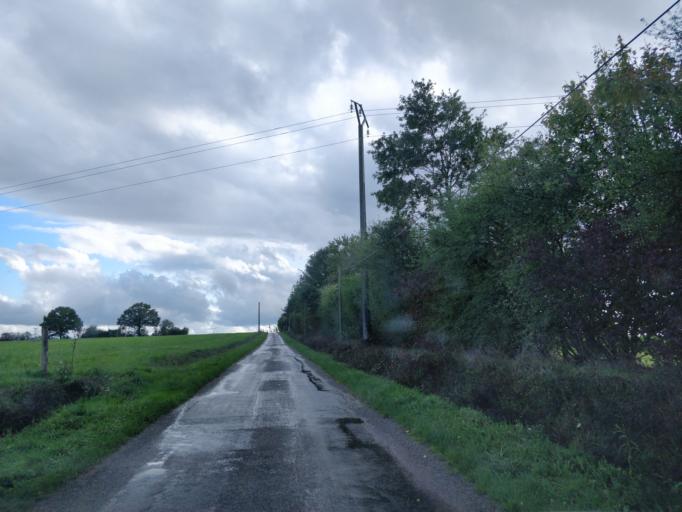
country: FR
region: Brittany
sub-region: Departement d'Ille-et-Vilaine
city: Chateaubourg
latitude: 48.1277
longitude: -1.4257
